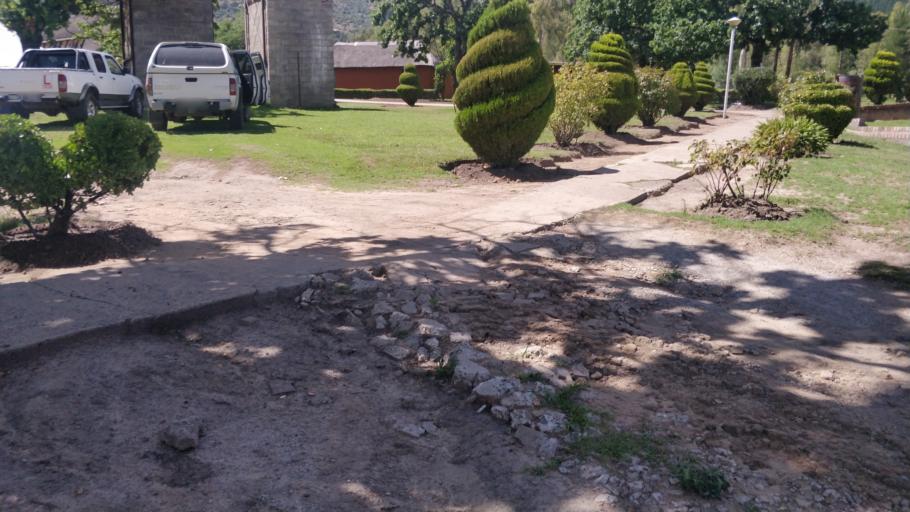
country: LS
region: Maseru
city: Nako
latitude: -29.6279
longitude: 27.5064
